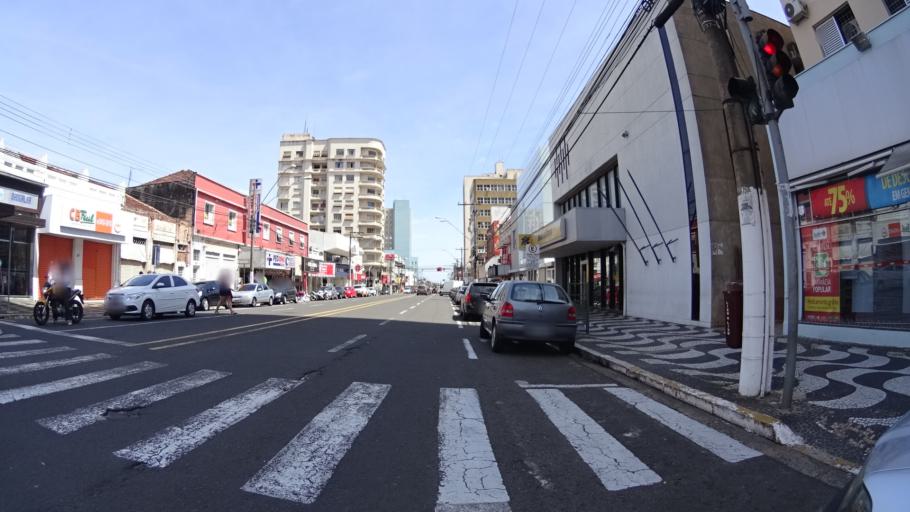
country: BR
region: Sao Paulo
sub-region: Marilia
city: Marilia
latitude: -22.2185
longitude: -49.9484
